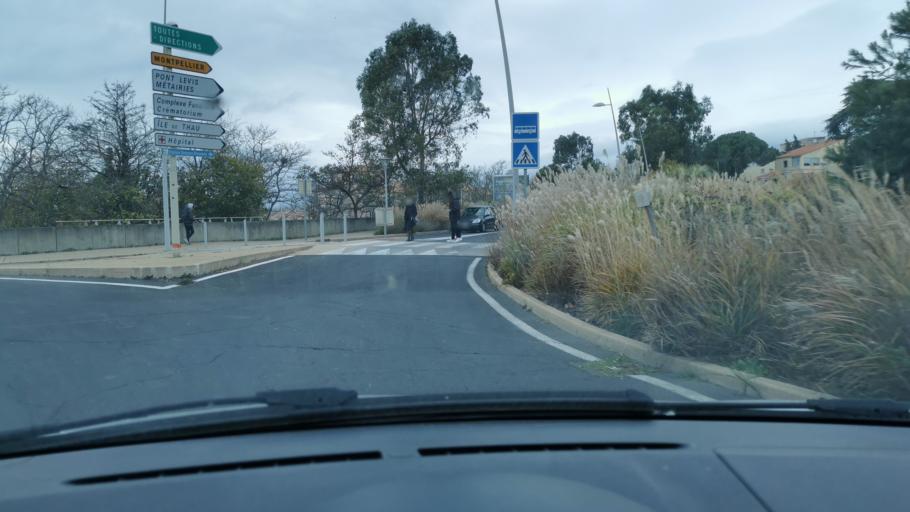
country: FR
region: Languedoc-Roussillon
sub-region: Departement de l'Herault
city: Sete
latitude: 43.3993
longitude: 3.6628
